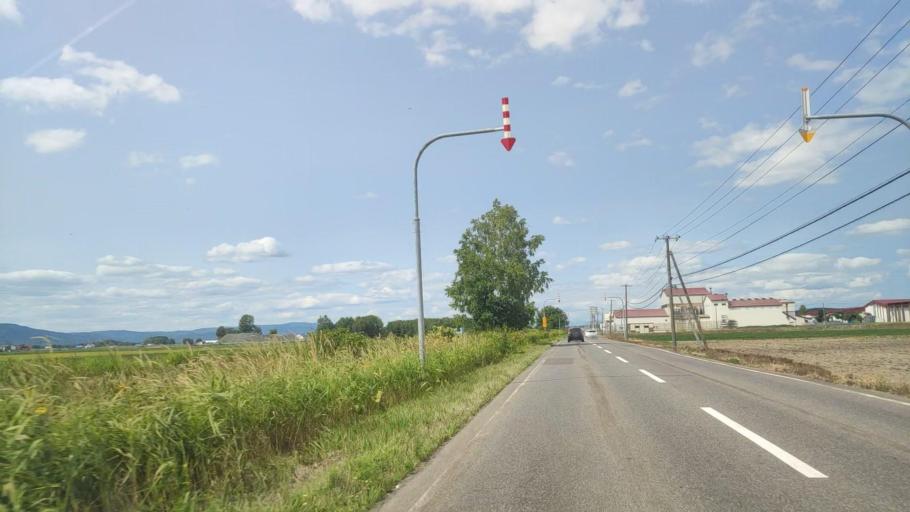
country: JP
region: Hokkaido
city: Nayoro
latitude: 44.2010
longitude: 142.4158
